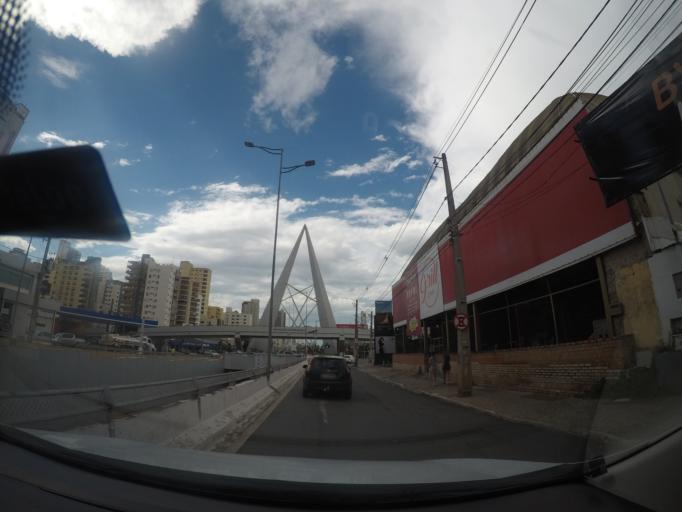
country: BR
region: Goias
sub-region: Goiania
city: Goiania
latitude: -16.7148
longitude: -49.2636
